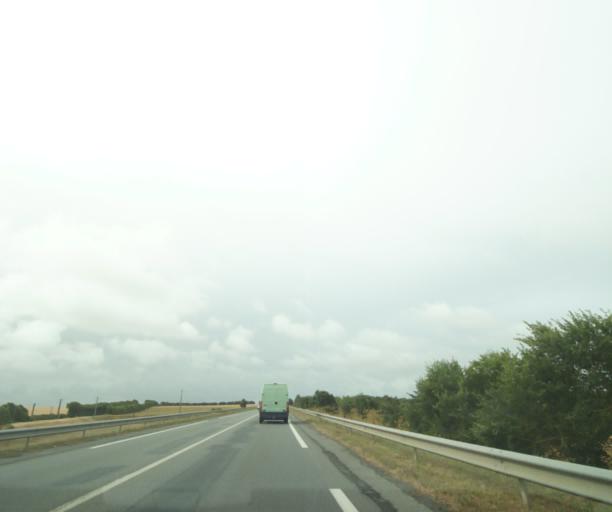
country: FR
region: Poitou-Charentes
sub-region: Departement de la Charente-Maritime
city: Marsilly
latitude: 46.2071
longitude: -1.1371
